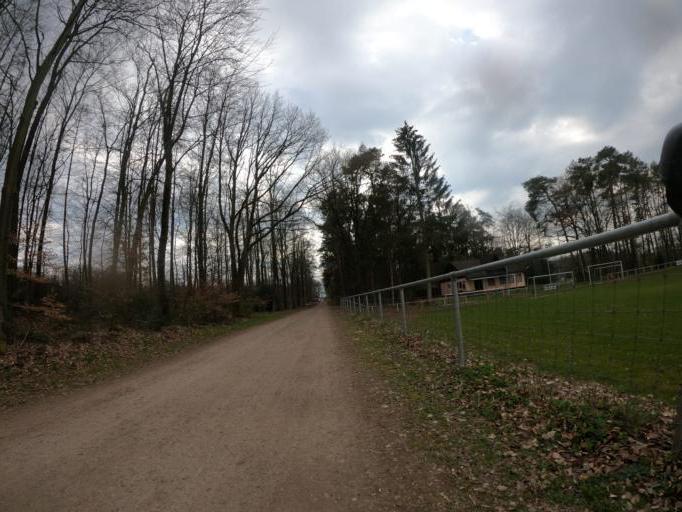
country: DE
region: North Rhine-Westphalia
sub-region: Regierungsbezirk Koln
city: Roetgen
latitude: 50.7061
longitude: 6.2231
